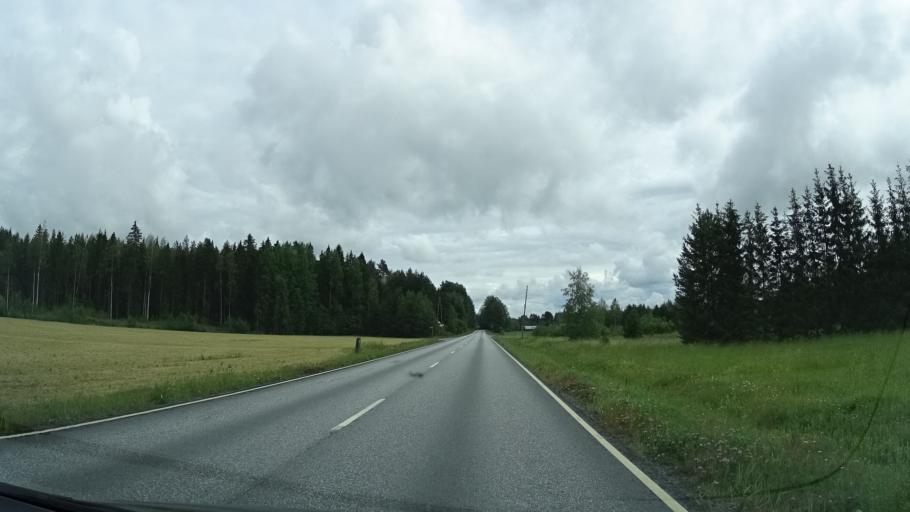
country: FI
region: Haeme
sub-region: Forssa
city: Humppila
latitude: 61.0951
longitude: 23.3633
